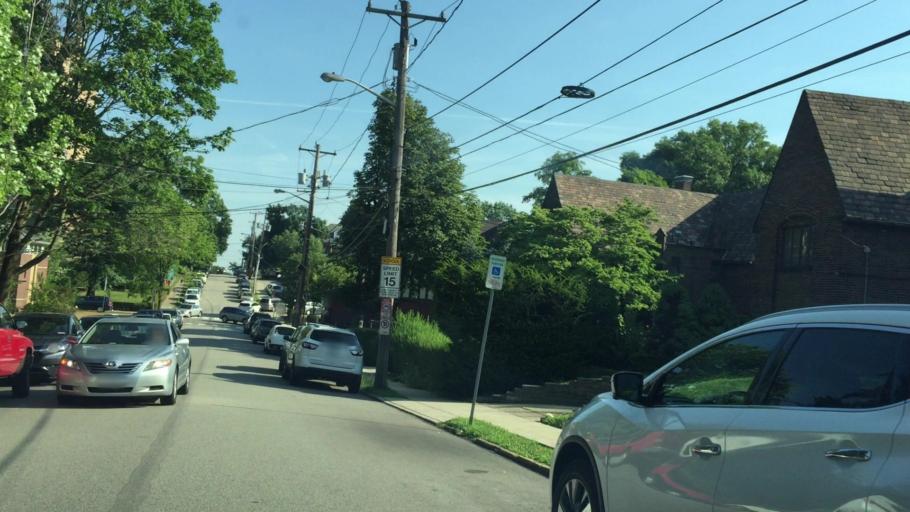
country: US
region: Pennsylvania
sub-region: Allegheny County
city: Homestead
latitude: 40.4371
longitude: -79.9176
